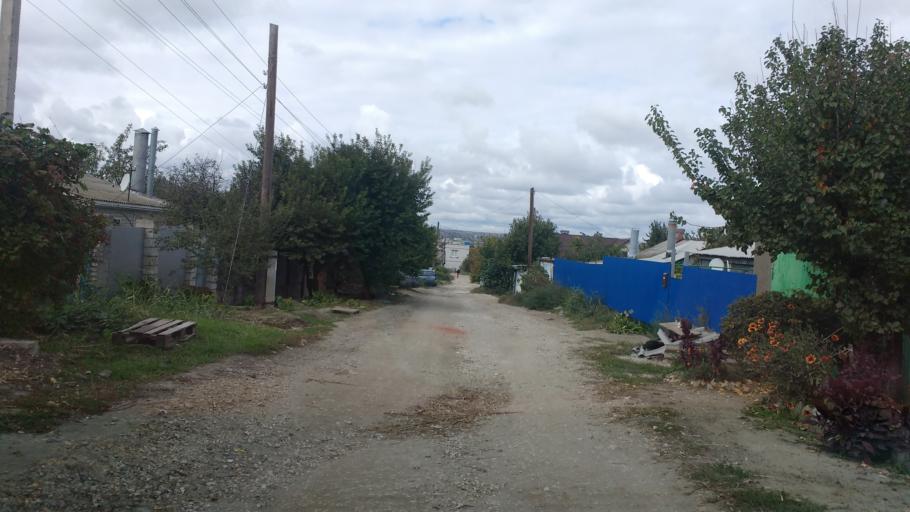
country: RU
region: Volgograd
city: Vodstroy
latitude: 48.7802
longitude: 44.5398
